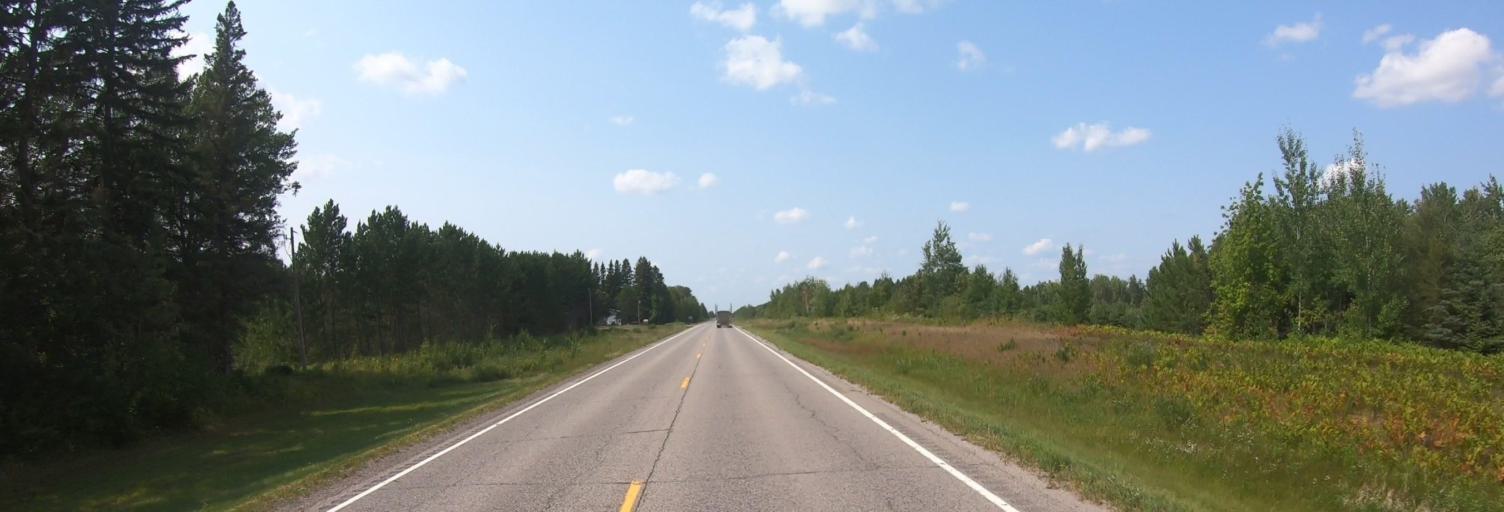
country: US
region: Minnesota
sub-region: Roseau County
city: Warroad
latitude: 48.8104
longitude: -95.1170
